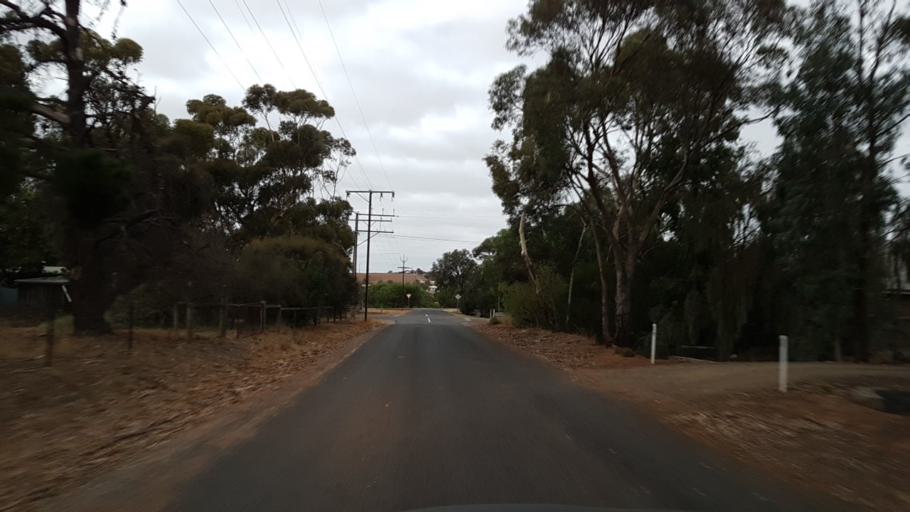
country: AU
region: South Australia
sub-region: Mount Barker
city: Callington
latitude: -35.0720
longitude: 139.0123
